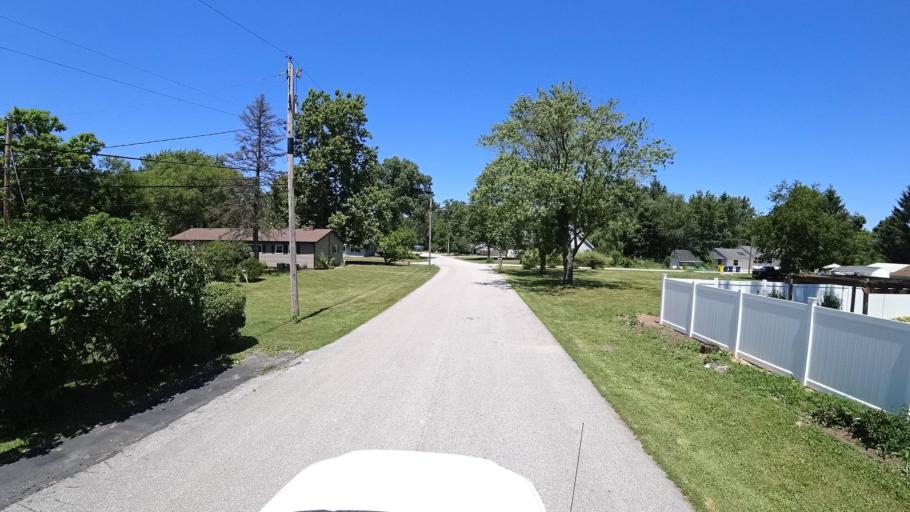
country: US
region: Indiana
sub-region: Porter County
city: Chesterton
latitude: 41.6171
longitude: -87.0539
